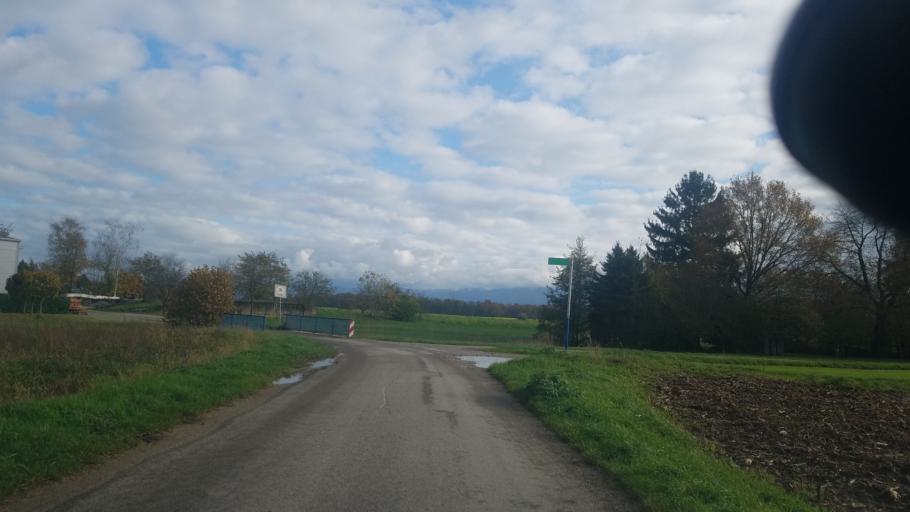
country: DE
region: Baden-Wuerttemberg
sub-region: Freiburg Region
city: Rheinau
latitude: 48.6747
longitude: 7.9832
